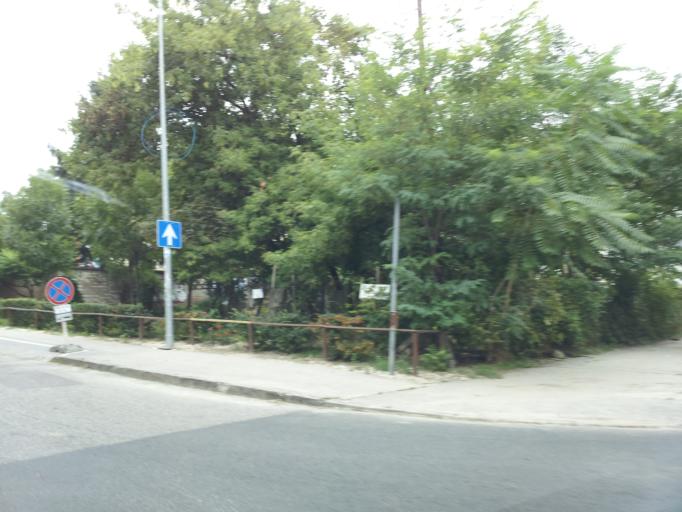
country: HU
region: Budapest
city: Budapest II. keruelet
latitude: 47.5252
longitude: 19.0378
